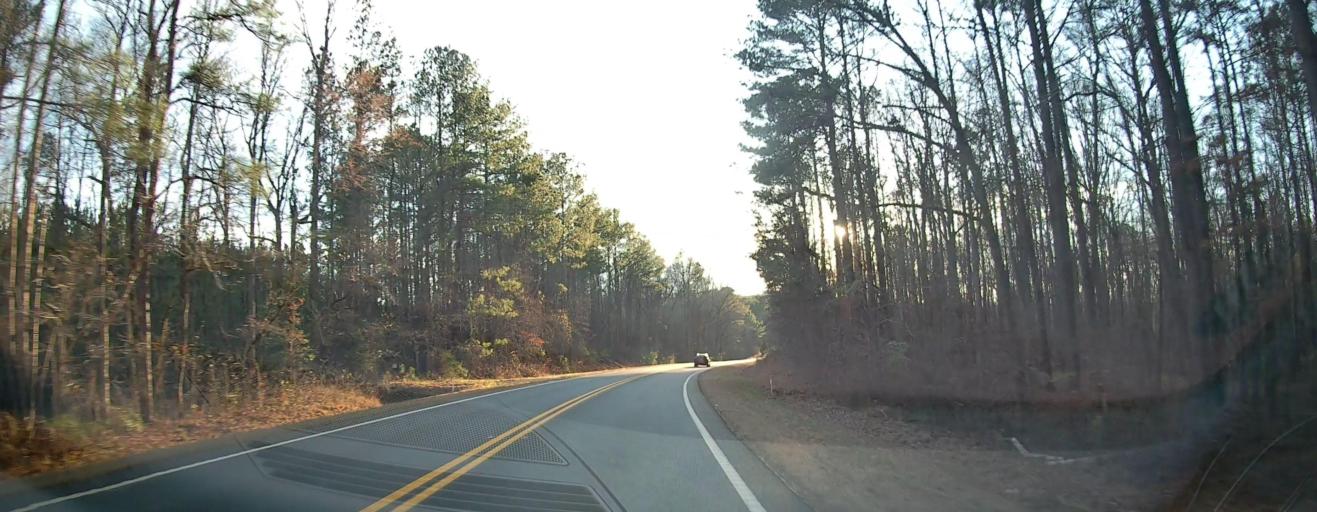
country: US
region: Georgia
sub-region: Talbot County
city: Sardis
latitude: 32.7083
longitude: -84.6903
